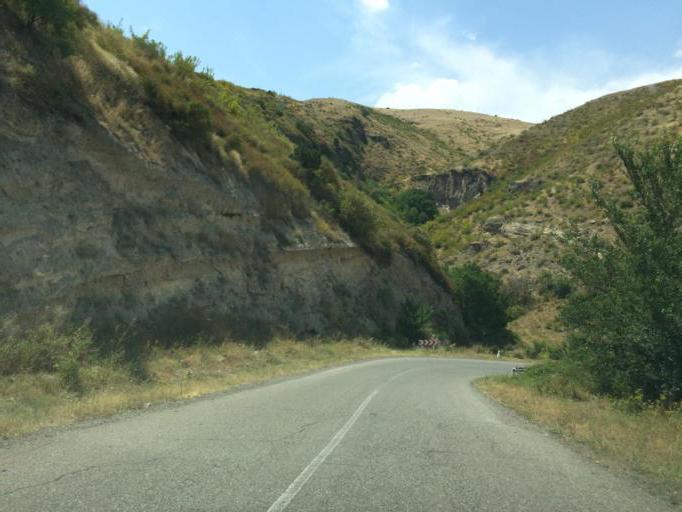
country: AZ
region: Lacin
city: Lacin
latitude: 39.5873
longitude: 46.5393
